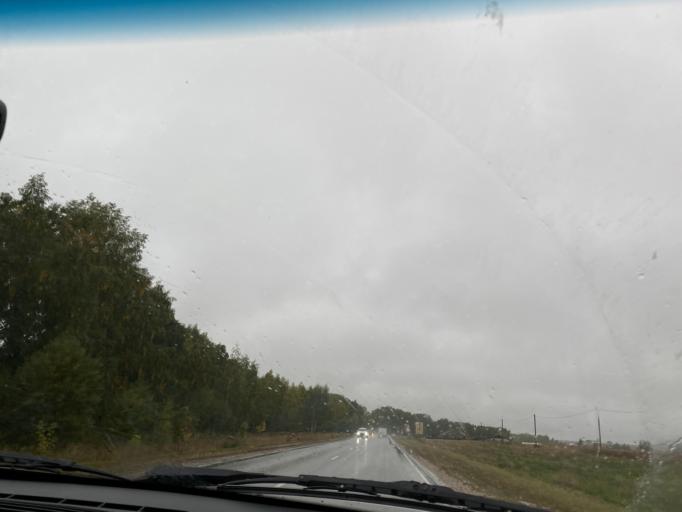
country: RU
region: Rjazan
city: Murmino
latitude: 54.4612
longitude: 39.8739
